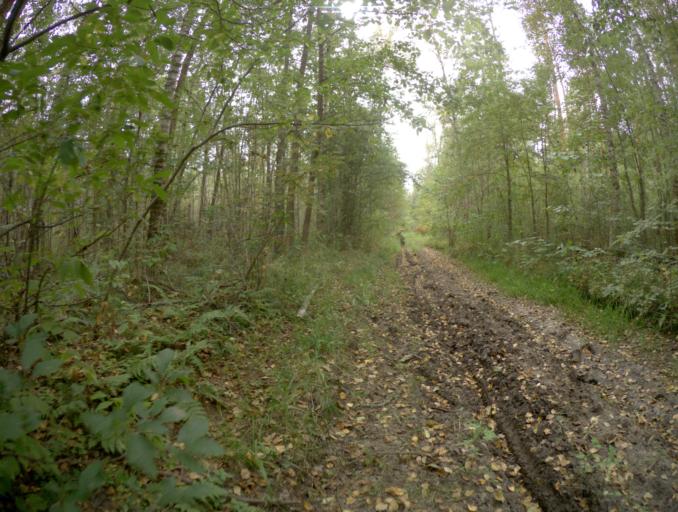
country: RU
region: Vladimir
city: Urshel'skiy
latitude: 55.8230
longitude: 40.2759
